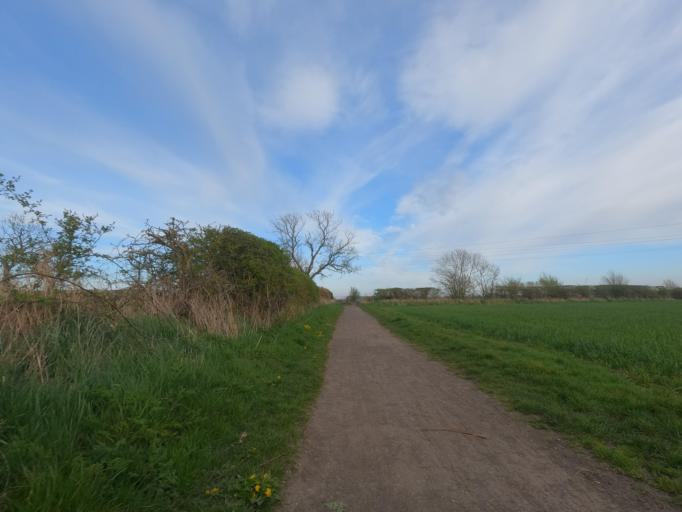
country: GB
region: England
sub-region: Newcastle upon Tyne
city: Hazlerigg
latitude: 55.0588
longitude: -1.6506
